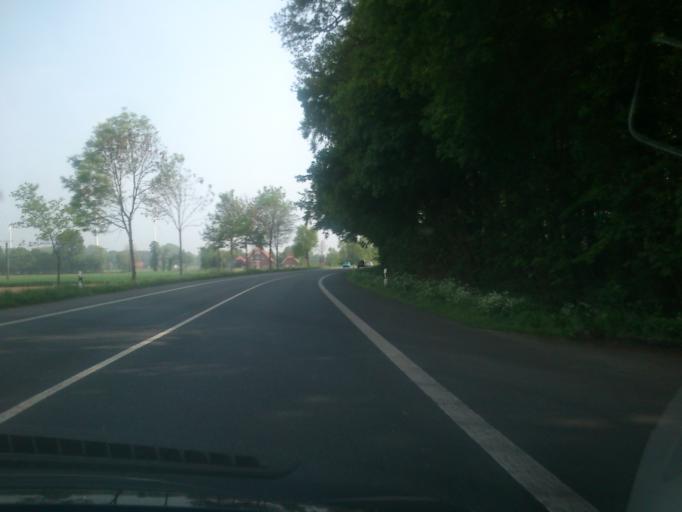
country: DE
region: North Rhine-Westphalia
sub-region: Regierungsbezirk Munster
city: Coesfeld
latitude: 51.8880
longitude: 7.2088
